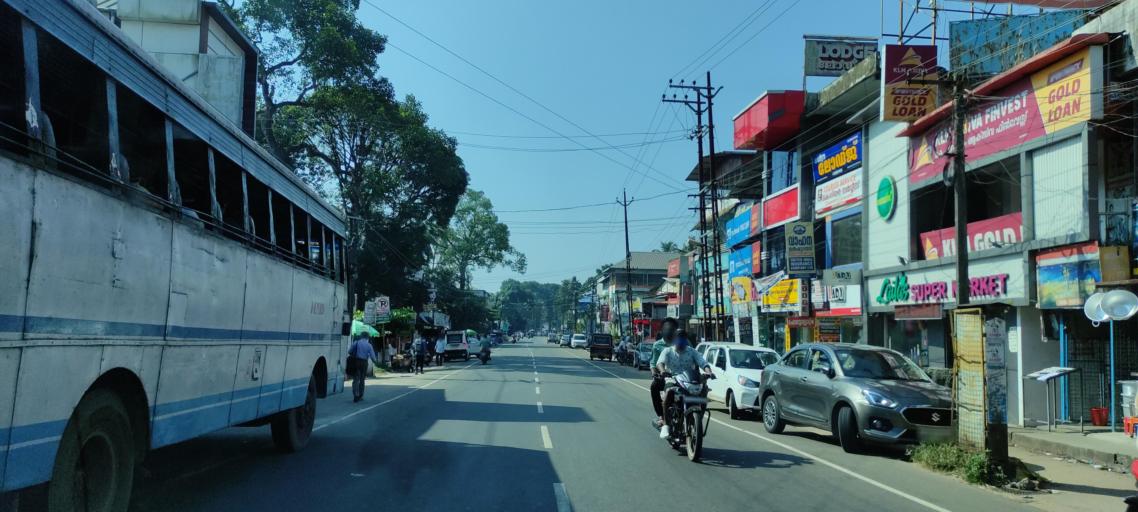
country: IN
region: Kerala
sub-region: Kollam
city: Panmana
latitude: 9.0592
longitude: 76.6381
